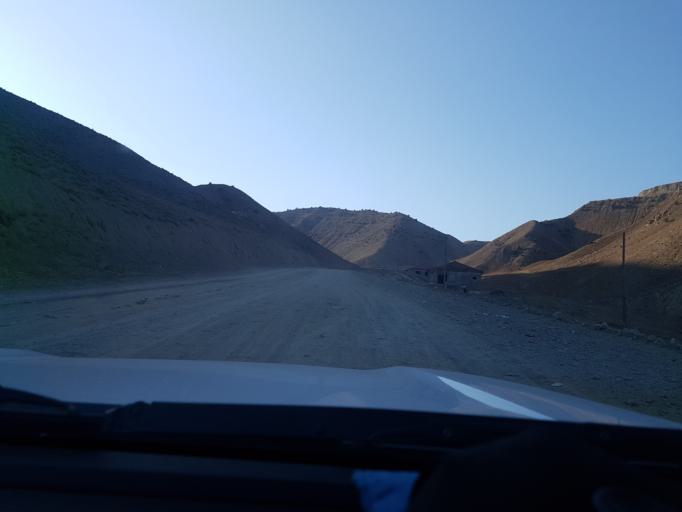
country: TM
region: Ahal
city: Baharly
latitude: 38.4513
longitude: 57.0464
